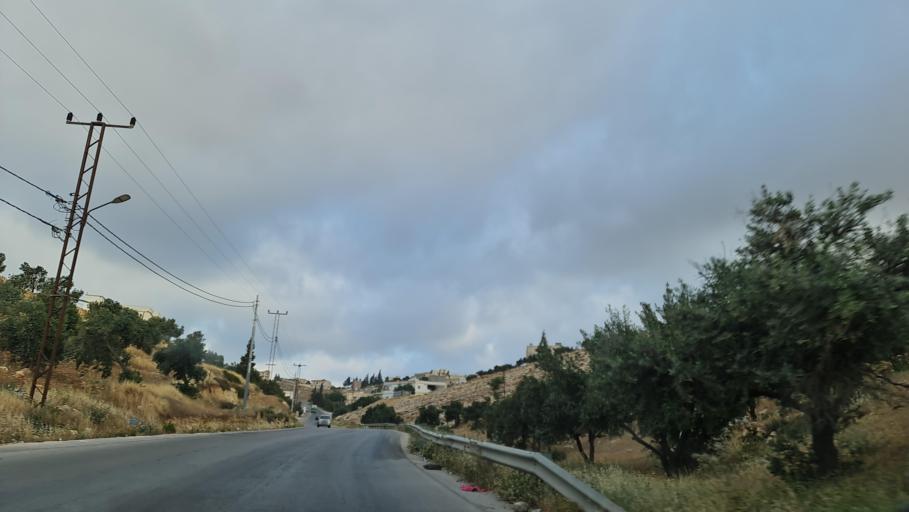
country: JO
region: Amman
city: Al Jubayhah
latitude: 32.0918
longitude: 35.9099
